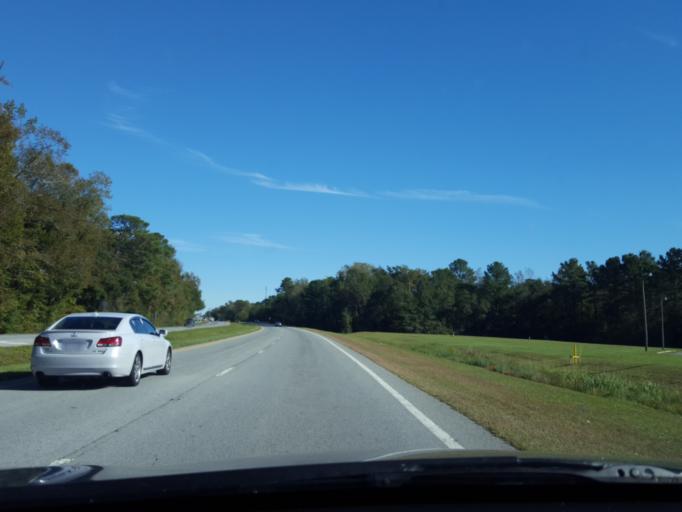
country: US
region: North Carolina
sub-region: Beaufort County
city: Washington
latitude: 35.6072
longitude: -77.1489
